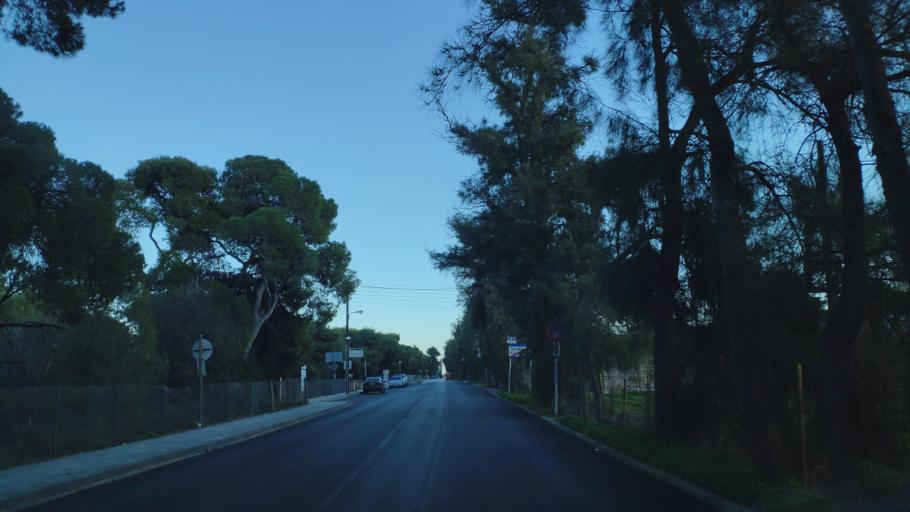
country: GR
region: Peloponnese
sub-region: Nomos Korinthias
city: Xylokastro
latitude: 38.0699
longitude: 22.6514
